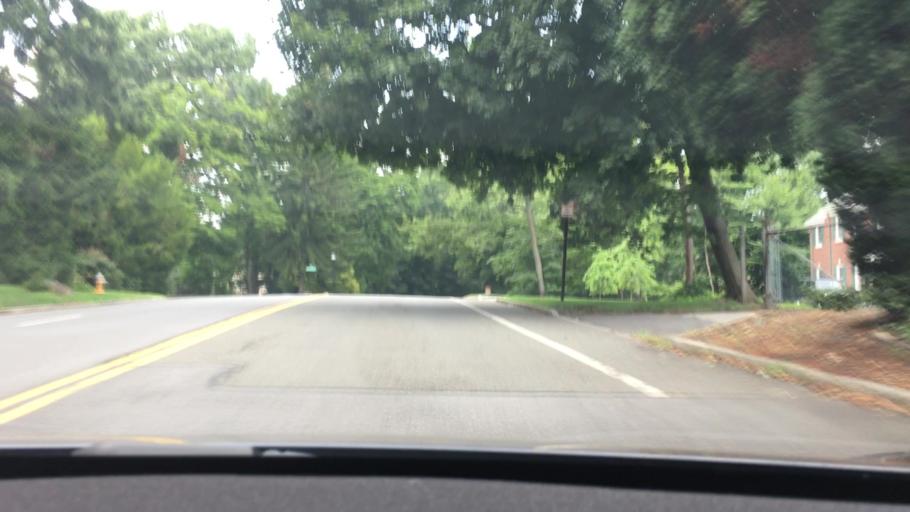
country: US
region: New York
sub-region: Westchester County
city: New Rochelle
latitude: 40.9277
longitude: -73.7883
